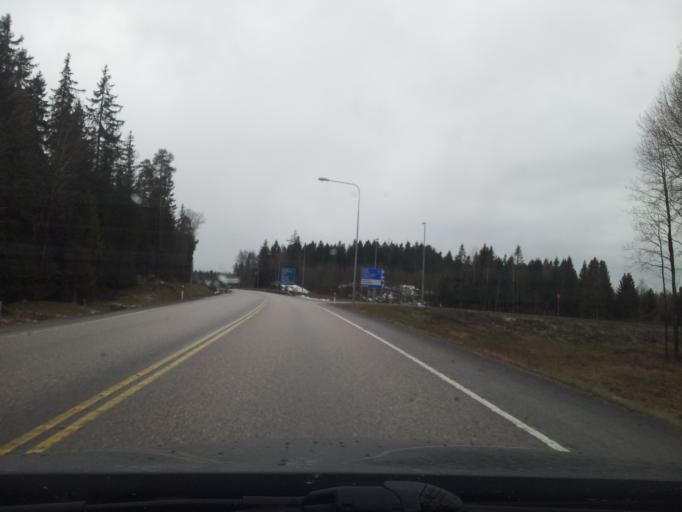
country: FI
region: Uusimaa
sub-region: Helsinki
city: Kirkkonummi
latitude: 60.1424
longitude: 24.5357
